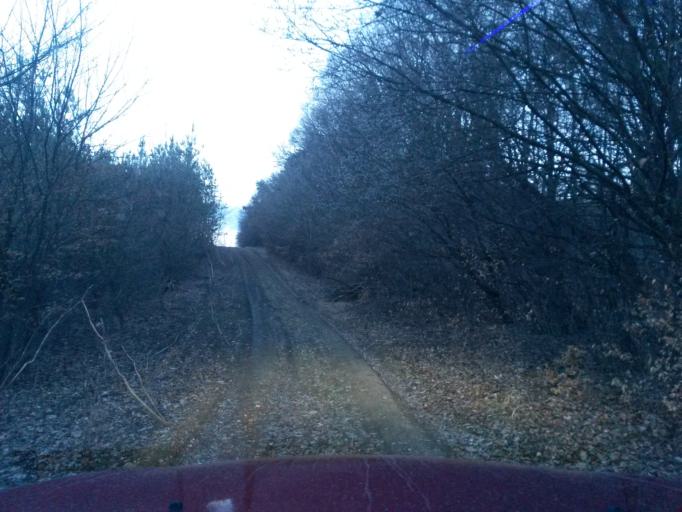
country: SK
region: Kosicky
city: Kosice
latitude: 48.6939
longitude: 21.3814
